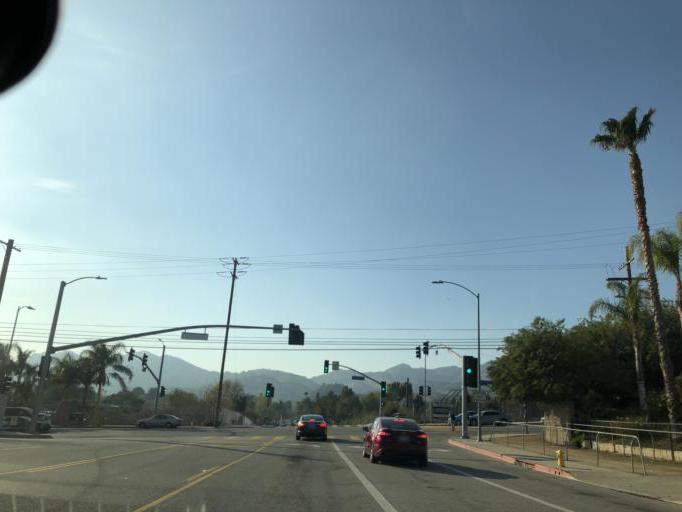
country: US
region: California
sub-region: Los Angeles County
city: Chatsworth
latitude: 34.2700
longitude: -118.5880
